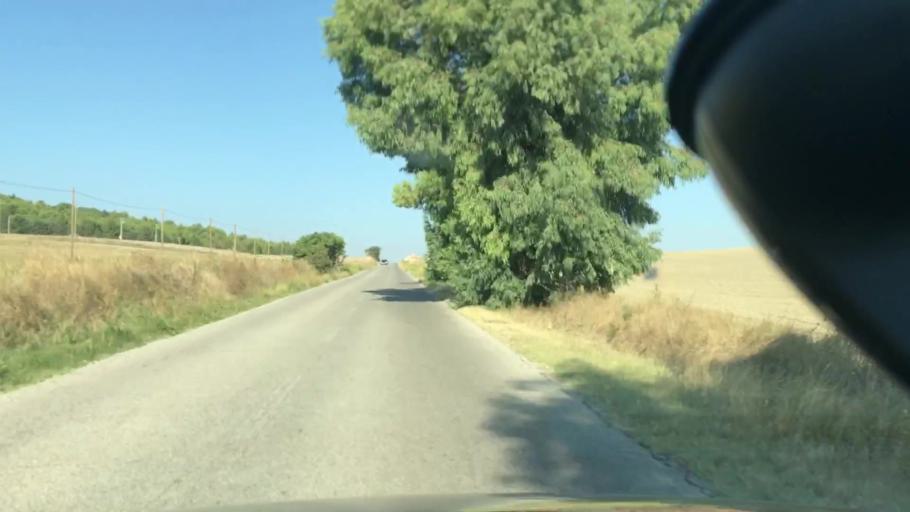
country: IT
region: Basilicate
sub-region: Provincia di Matera
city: La Martella
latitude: 40.6644
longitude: 16.4973
